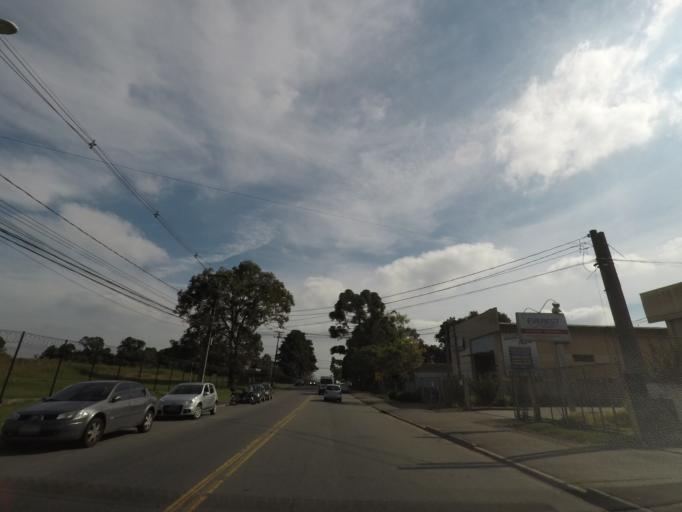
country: BR
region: Parana
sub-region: Sao Jose Dos Pinhais
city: Sao Jose dos Pinhais
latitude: -25.5105
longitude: -49.2552
